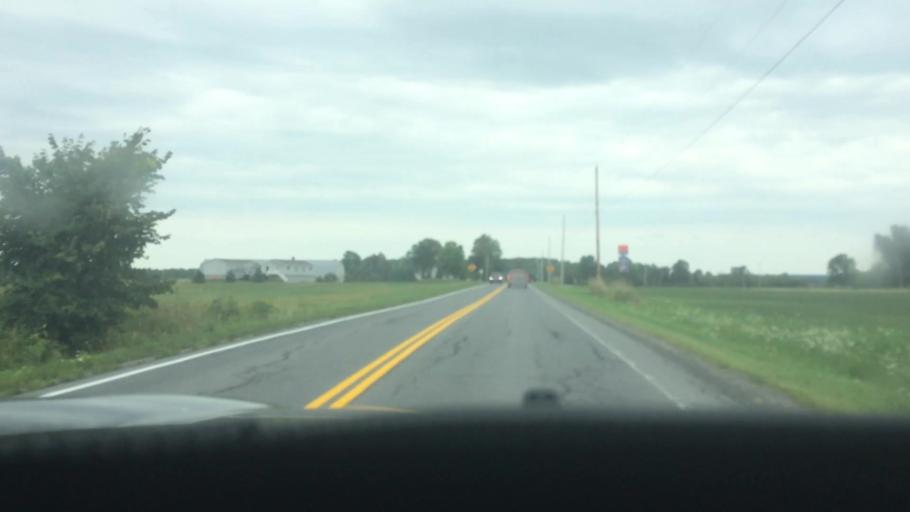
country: US
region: New York
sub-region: St. Lawrence County
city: Canton
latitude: 44.5517
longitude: -75.1398
